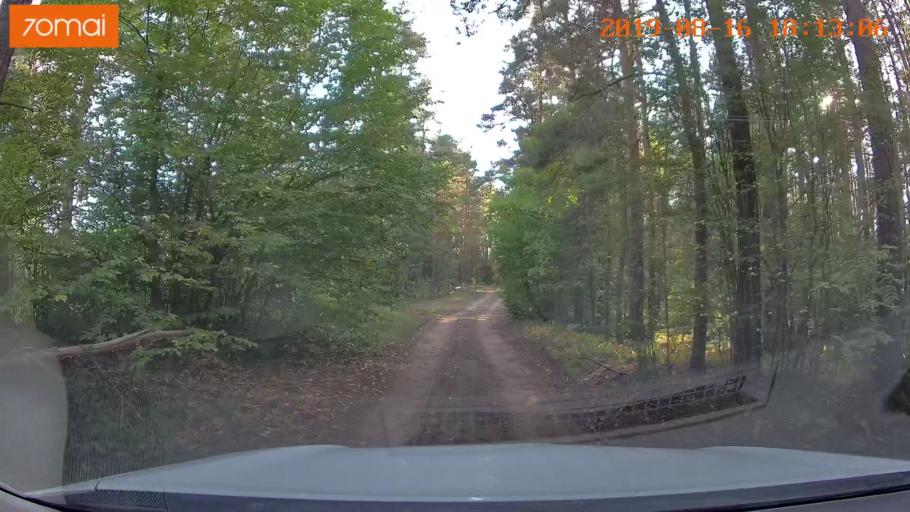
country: BY
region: Mogilev
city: Asipovichy
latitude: 53.2125
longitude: 28.6446
